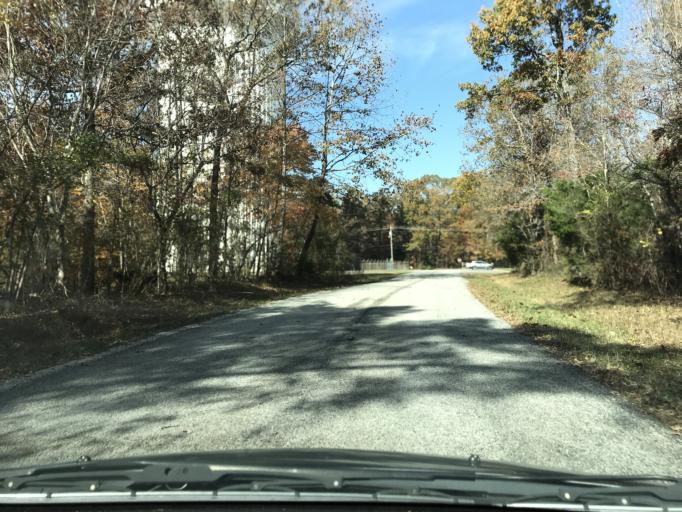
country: US
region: Tennessee
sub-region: Coffee County
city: Tullahoma
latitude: 35.4064
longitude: -86.1738
